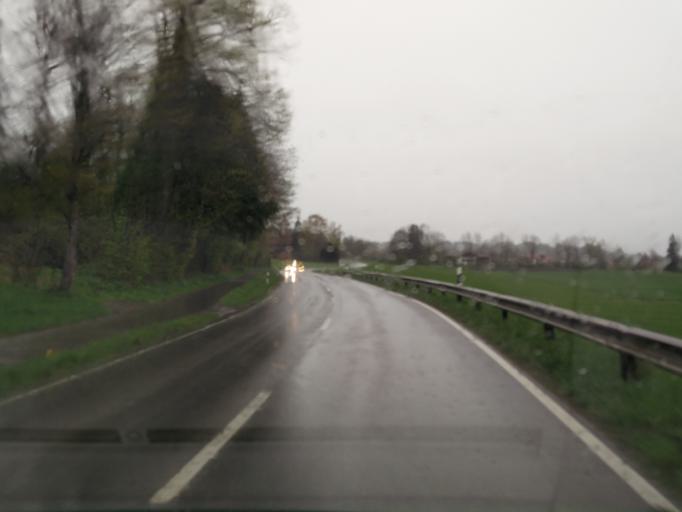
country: DE
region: Bavaria
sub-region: Upper Bavaria
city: Bernau am Chiemsee
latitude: 47.8019
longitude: 12.3883
